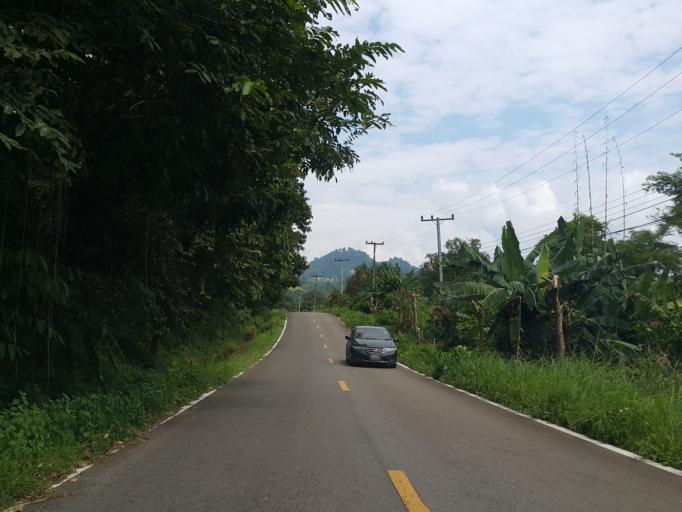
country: TH
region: Mae Hong Son
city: Mae Hong Son
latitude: 19.4734
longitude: 97.9657
